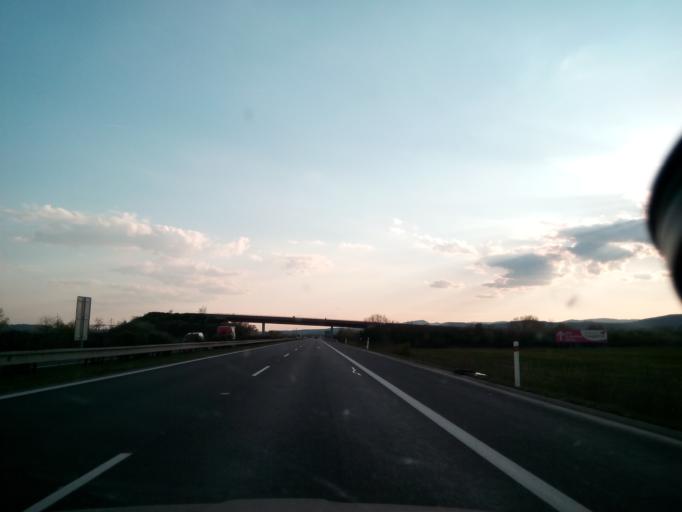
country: SK
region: Nitriansky
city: Dubnica nad Vahom
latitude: 48.9741
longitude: 18.1663
